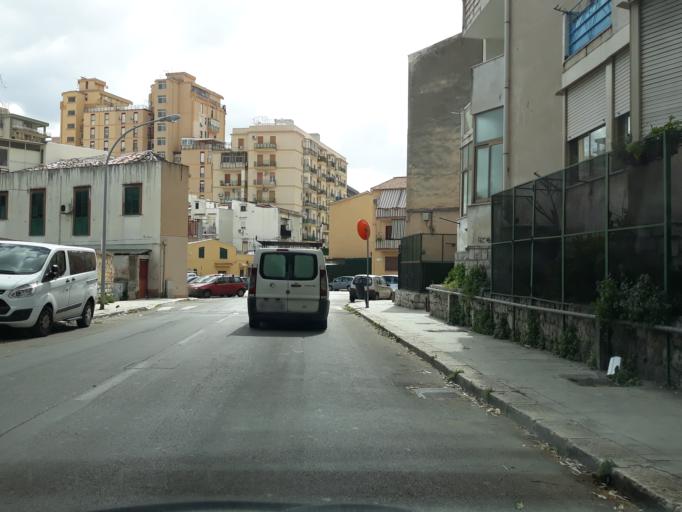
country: IT
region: Sicily
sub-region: Palermo
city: Palermo
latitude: 38.1164
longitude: 13.3391
